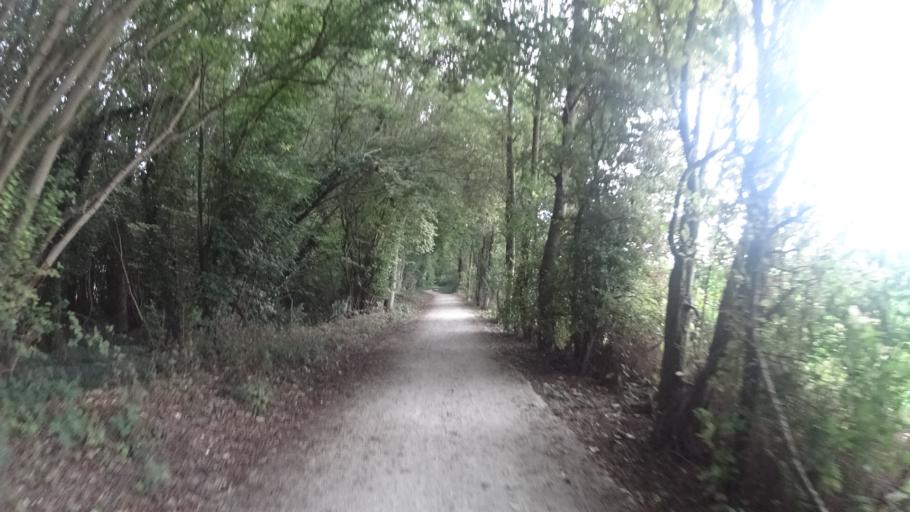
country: FR
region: Picardie
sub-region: Departement de l'Aisne
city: Origny-Sainte-Benoite
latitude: 49.8505
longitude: 3.4979
